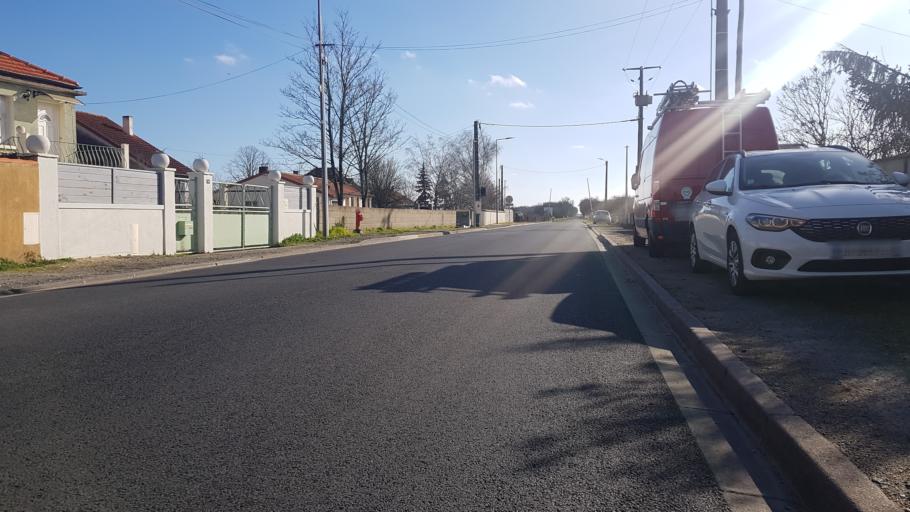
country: FR
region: Poitou-Charentes
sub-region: Departement de la Vienne
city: Avanton
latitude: 46.6581
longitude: 0.3048
